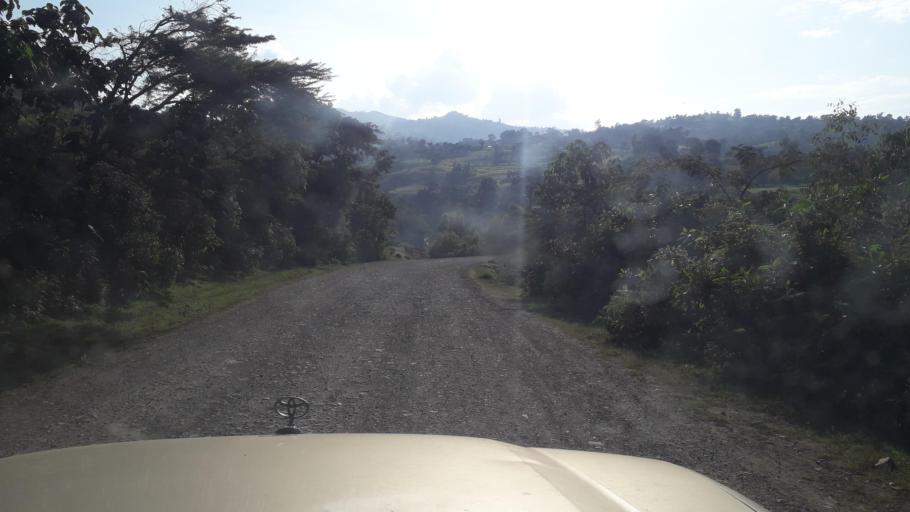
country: ET
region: Oromiya
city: Jima
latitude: 7.4768
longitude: 36.8784
